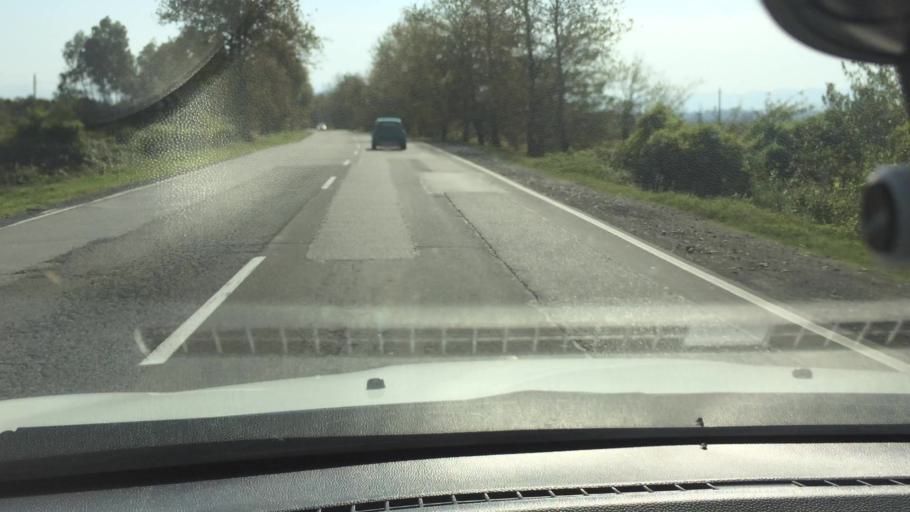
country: GE
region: Guria
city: Urek'i
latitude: 42.0210
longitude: 41.7598
